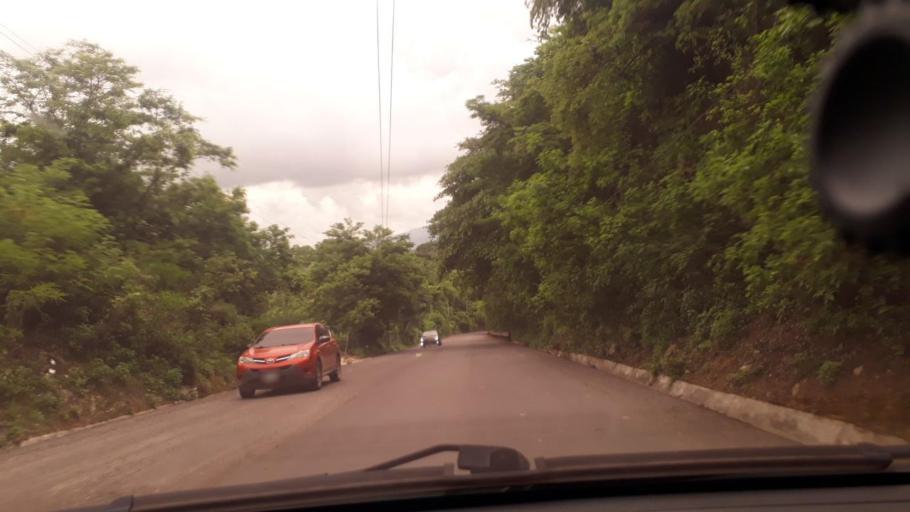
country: GT
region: Chiquimula
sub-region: Municipio de San Juan Ermita
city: San Juan Ermita
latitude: 14.7459
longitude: -89.4606
